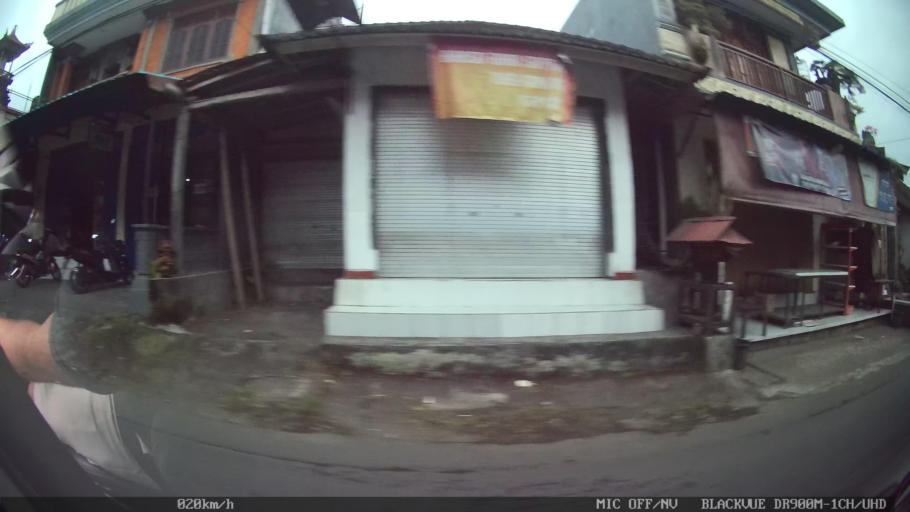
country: ID
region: Bali
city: Banjar Triwangsakeliki
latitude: -8.4482
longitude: 115.2628
